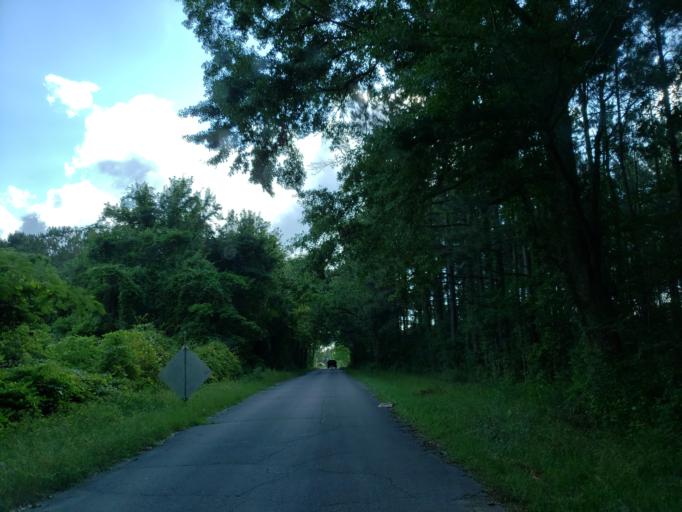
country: US
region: Mississippi
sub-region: Forrest County
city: Petal
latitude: 31.3176
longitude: -89.2007
